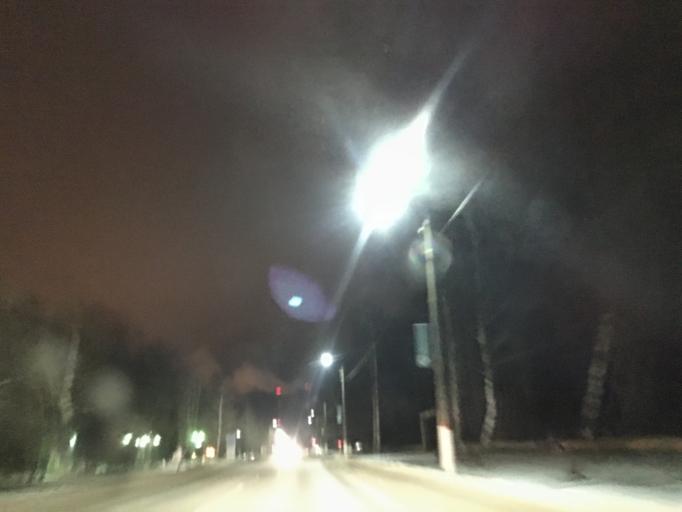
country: RU
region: Tula
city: Pervomayskiy
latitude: 54.0369
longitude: 37.5205
